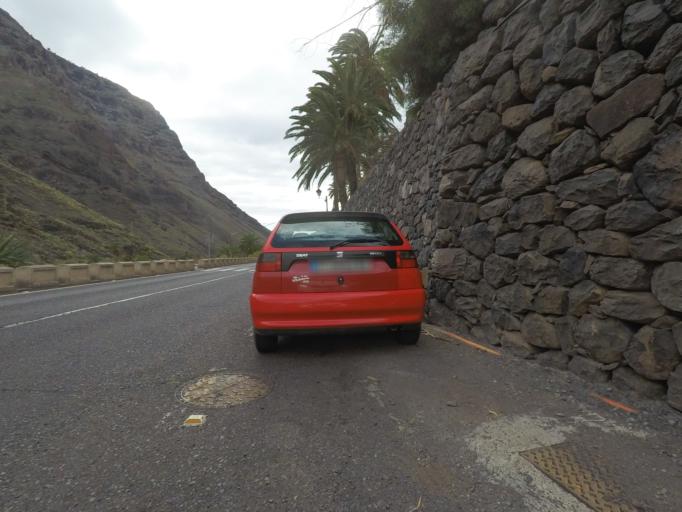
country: ES
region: Canary Islands
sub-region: Provincia de Santa Cruz de Tenerife
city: Vallehermosa
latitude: 28.1045
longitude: -17.3276
